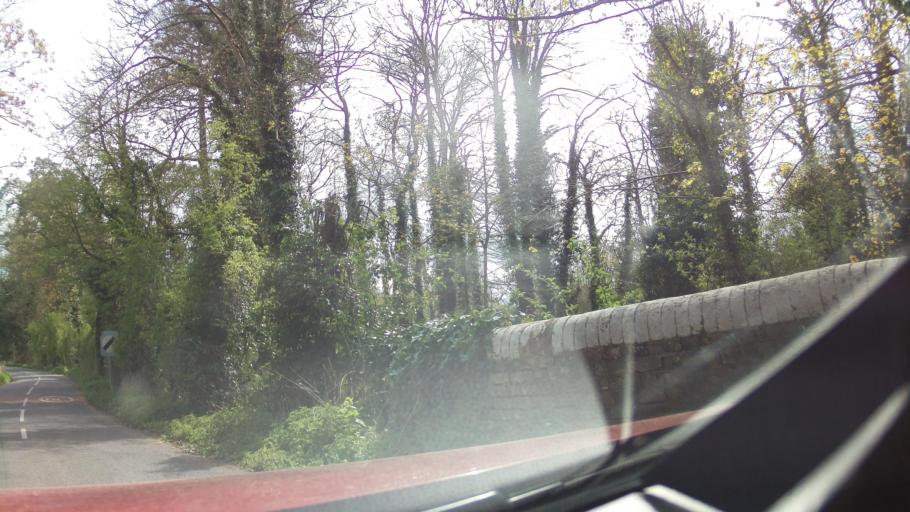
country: GB
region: England
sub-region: Hampshire
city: Romsey
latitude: 51.0790
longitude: -1.5161
